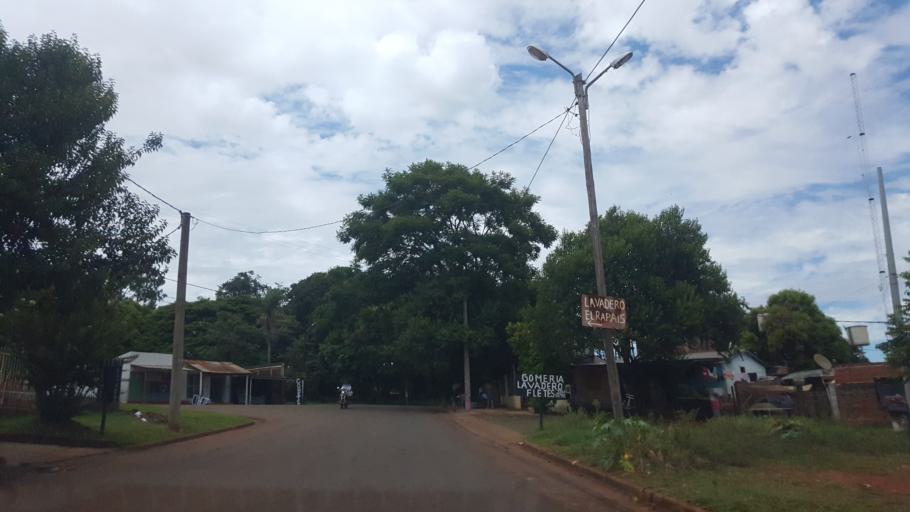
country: AR
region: Misiones
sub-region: Departamento de Capital
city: Posadas
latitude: -27.4257
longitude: -55.8866
